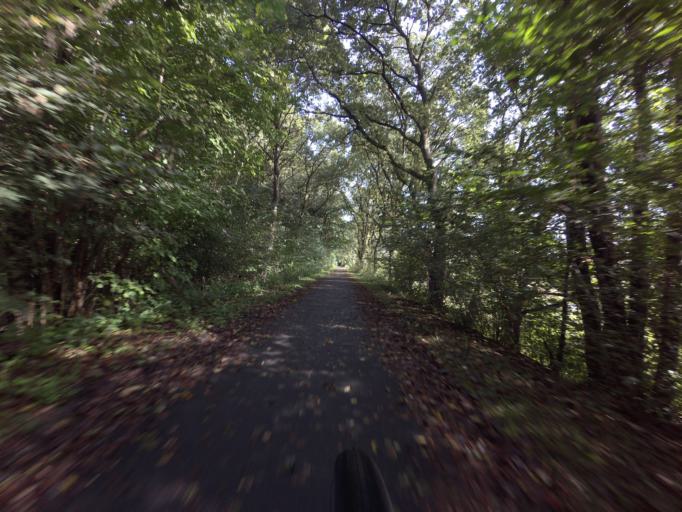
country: DK
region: Central Jutland
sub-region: Viborg Kommune
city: Viborg
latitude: 56.4321
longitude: 9.4609
